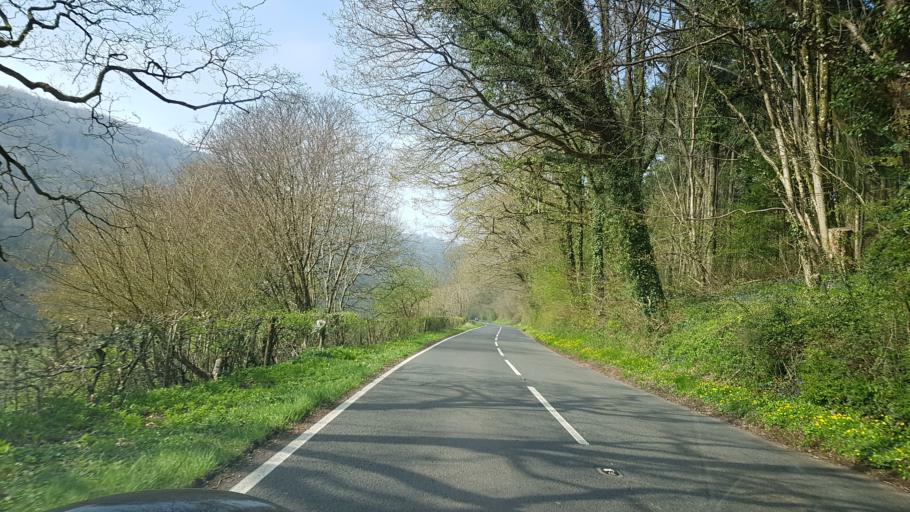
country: GB
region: Wales
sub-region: Monmouthshire
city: Tintern
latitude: 51.7602
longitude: -2.6703
